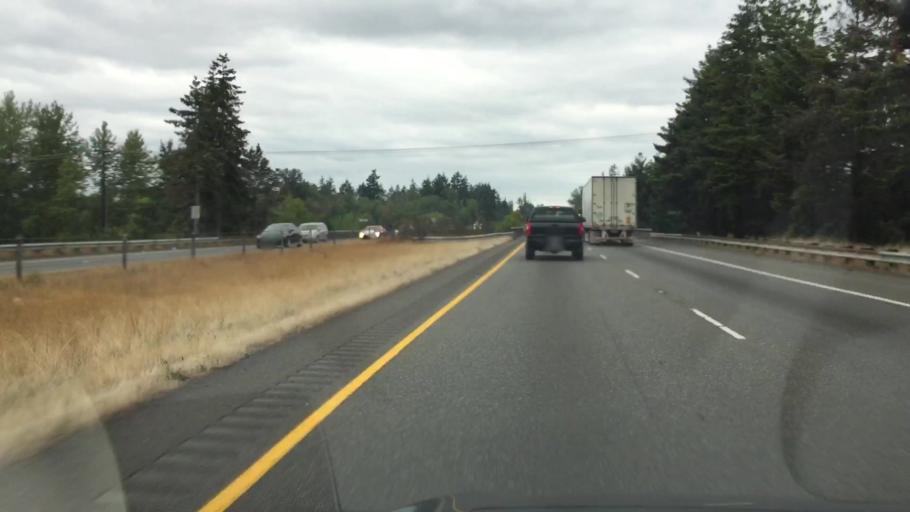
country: US
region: Washington
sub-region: Pierce County
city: Midland
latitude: 47.1583
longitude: -122.3877
